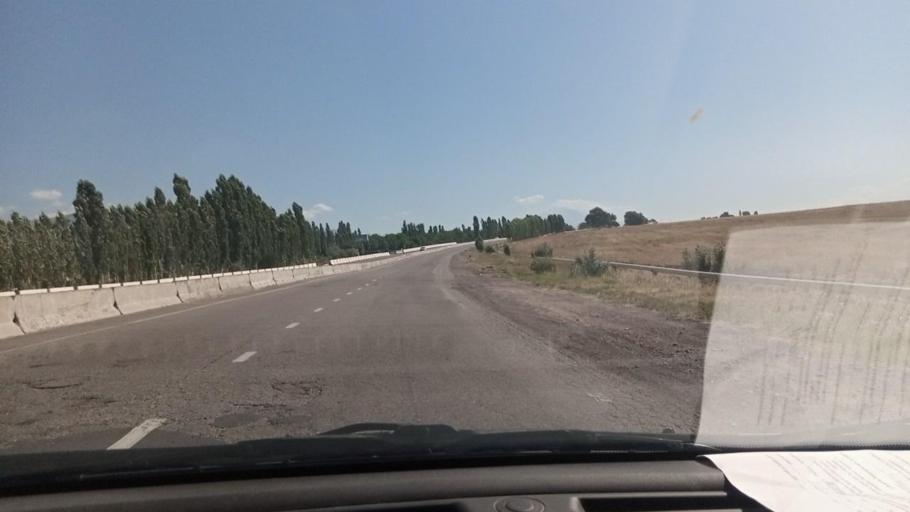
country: UZ
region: Toshkent
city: Angren
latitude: 40.9465
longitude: 69.9080
